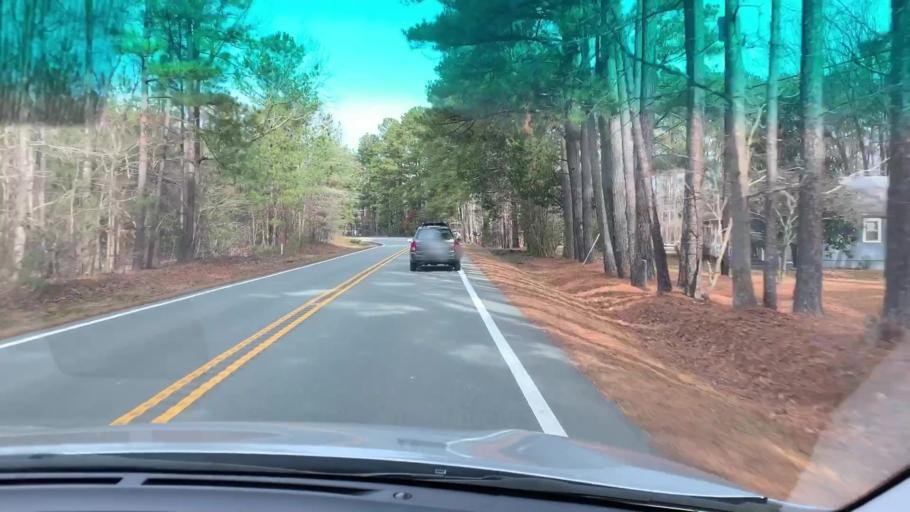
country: US
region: North Carolina
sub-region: Wake County
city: Green Level
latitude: 35.8604
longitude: -78.9414
